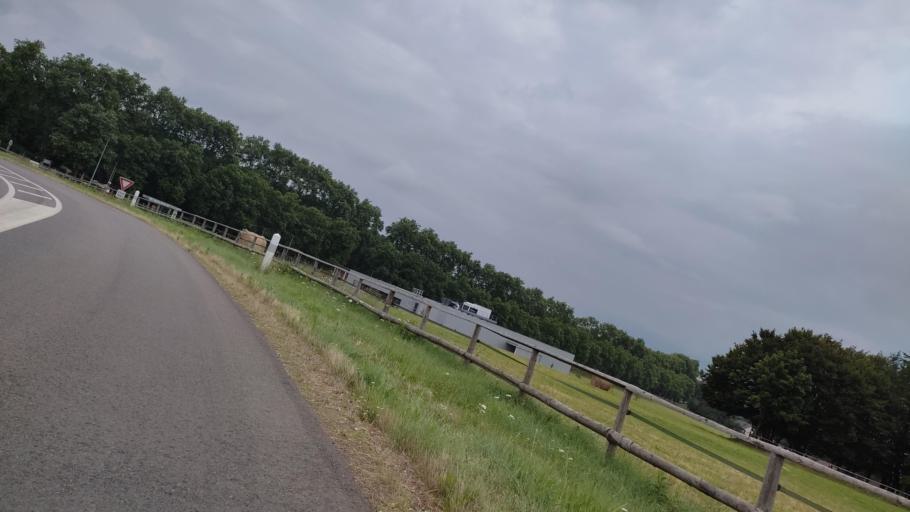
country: FR
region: Bourgogne
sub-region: Departement de la Nievre
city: Chatillon-en-Bazois
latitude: 47.0441
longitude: 3.6442
